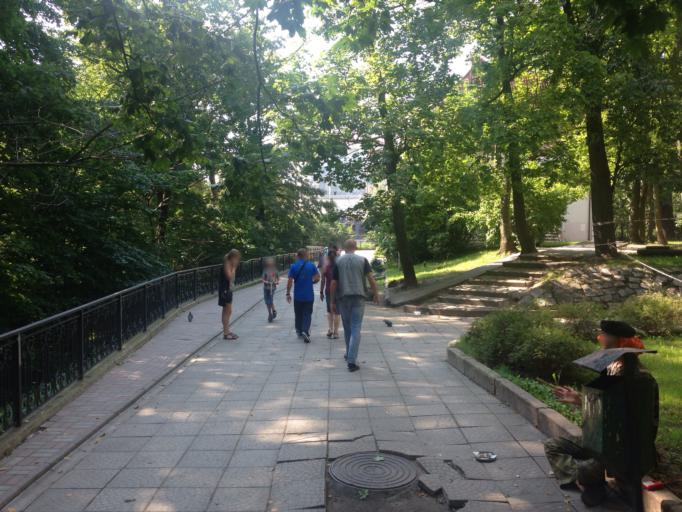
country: RU
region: Kaliningrad
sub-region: Gorod Kaliningrad
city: Kaliningrad
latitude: 54.7204
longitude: 20.4867
